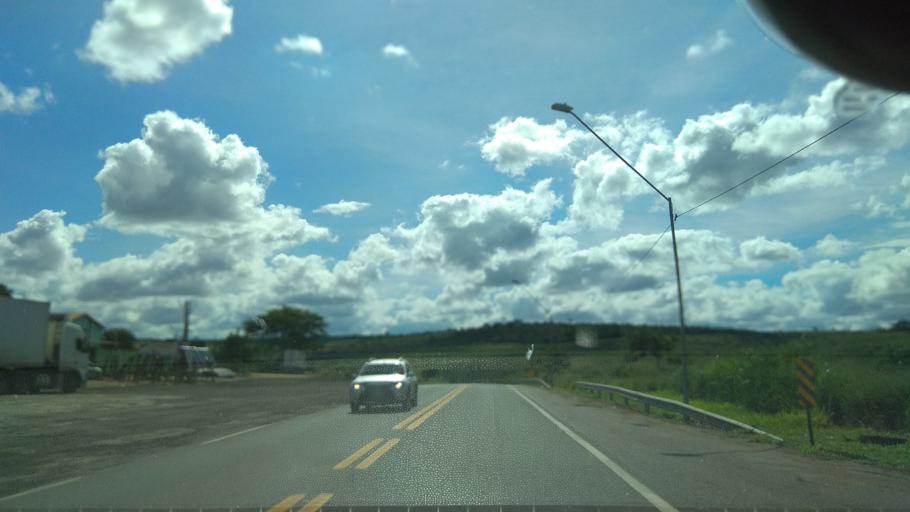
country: BR
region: Bahia
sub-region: Santa Ines
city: Santa Ines
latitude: -13.2278
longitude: -40.0178
